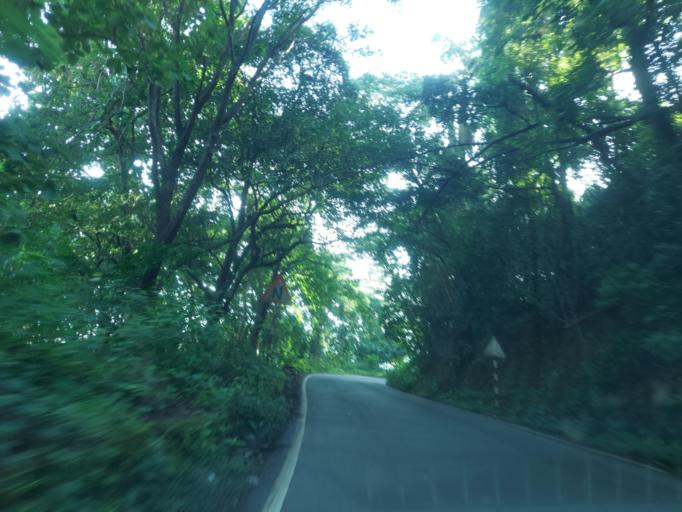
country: IN
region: Maharashtra
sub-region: Sindhudurg
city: Savantvadi
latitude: 15.9366
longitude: 73.9450
